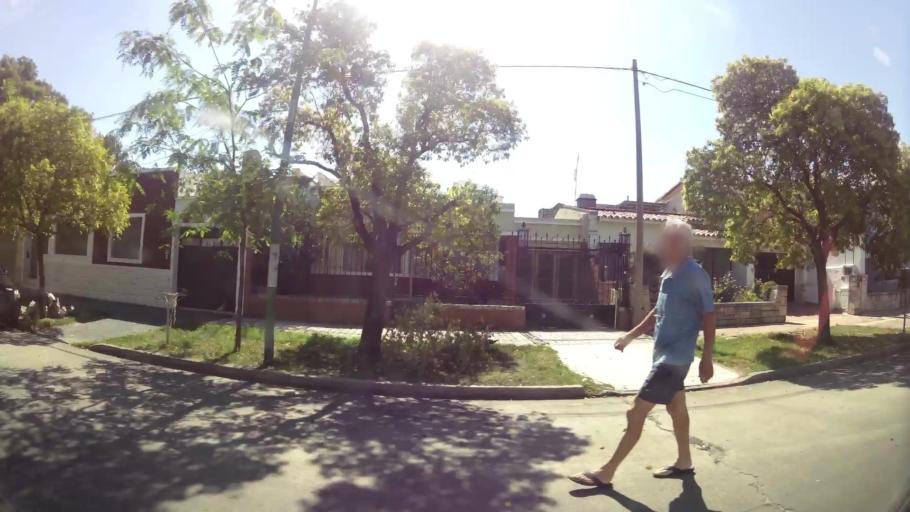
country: AR
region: Cordoba
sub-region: Departamento de Capital
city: Cordoba
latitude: -31.4207
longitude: -64.1687
